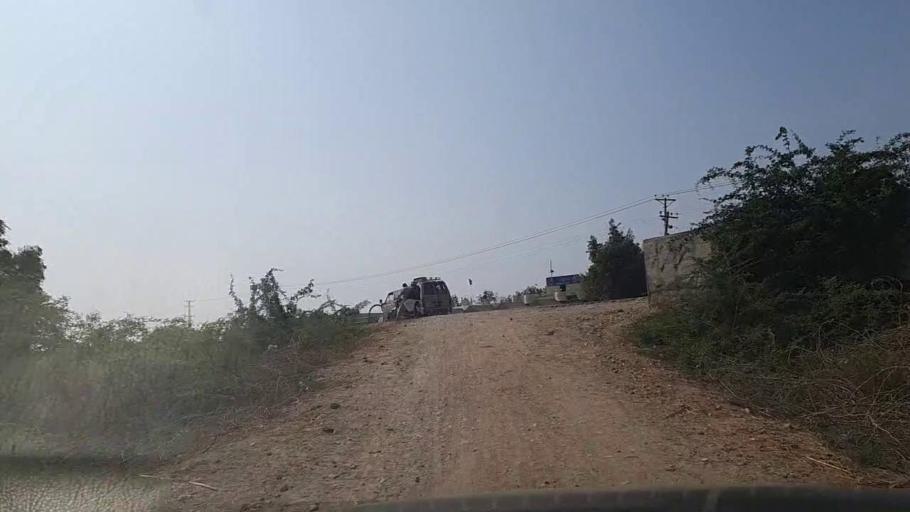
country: PK
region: Sindh
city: Gharo
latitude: 24.6765
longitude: 67.5909
